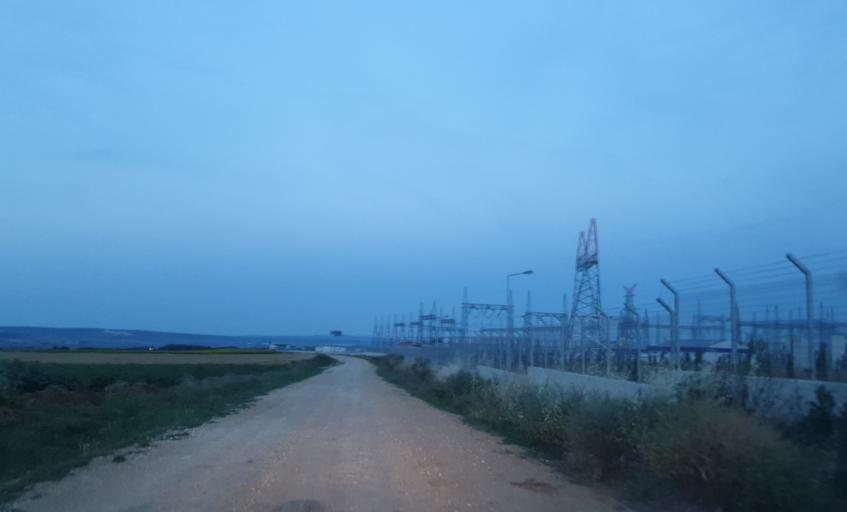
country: TR
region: Kirklareli
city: Vize
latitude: 41.5177
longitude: 27.7559
